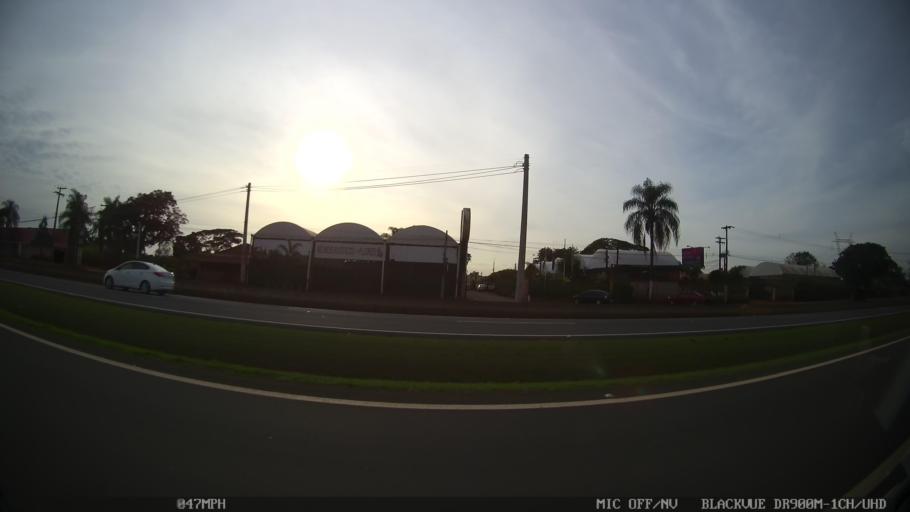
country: BR
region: Sao Paulo
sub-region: Iracemapolis
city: Iracemapolis
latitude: -22.5964
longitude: -47.4685
